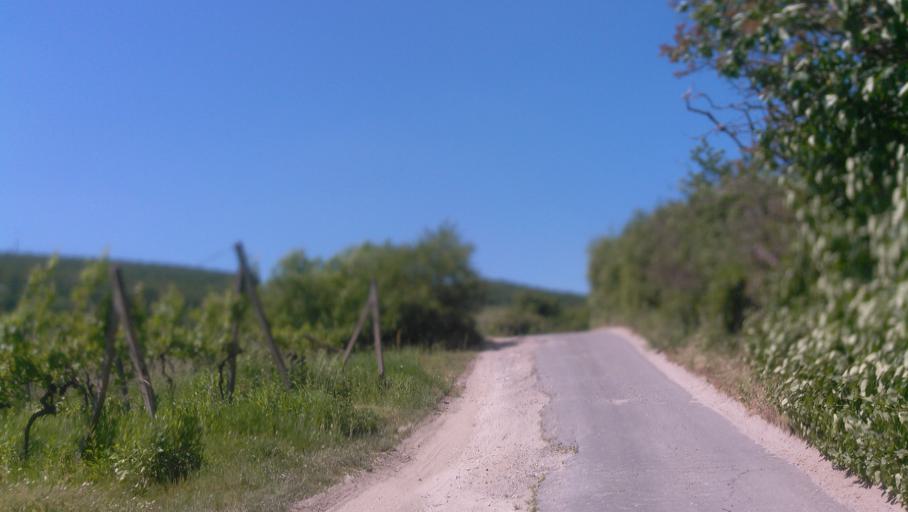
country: SK
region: Bratislavsky
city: Bratislava
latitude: 48.1844
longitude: 17.1249
